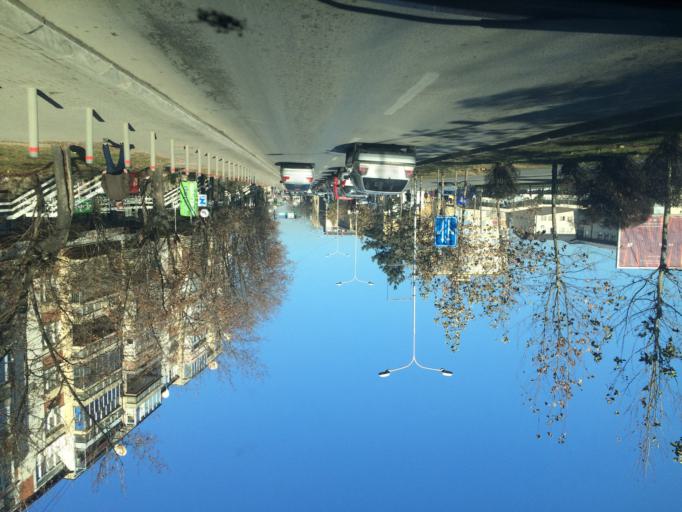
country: XK
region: Pristina
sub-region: Komuna e Prishtines
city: Pristina
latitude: 42.6579
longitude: 21.1645
